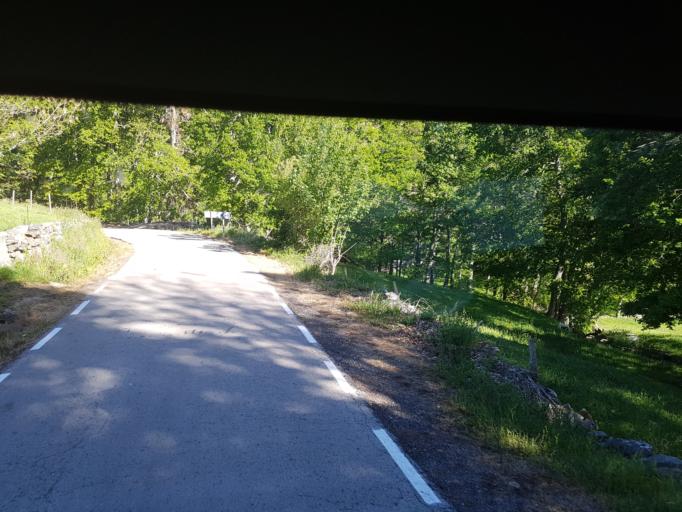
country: ES
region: Castille and Leon
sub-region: Provincia de Burgos
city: Espinosa de los Monteros
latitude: 43.1214
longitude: -3.5805
